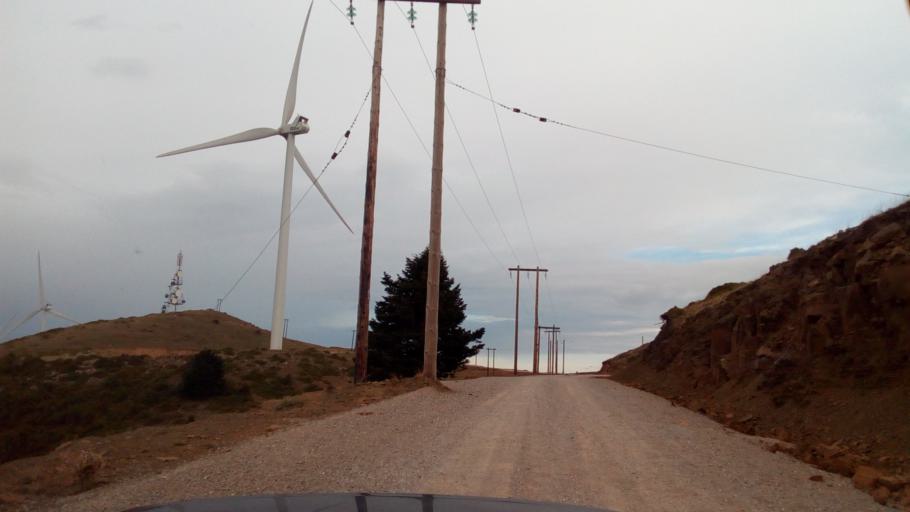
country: GR
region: Central Greece
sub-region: Nomos Fokidos
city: Lidoriki
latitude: 38.4567
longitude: 22.0739
